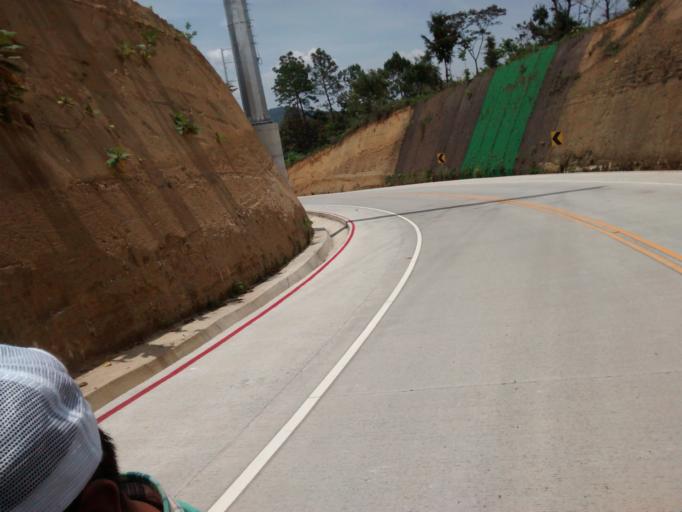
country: GT
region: Sacatepequez
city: Santo Domingo Xenacoj
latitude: 14.6796
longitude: -90.7144
